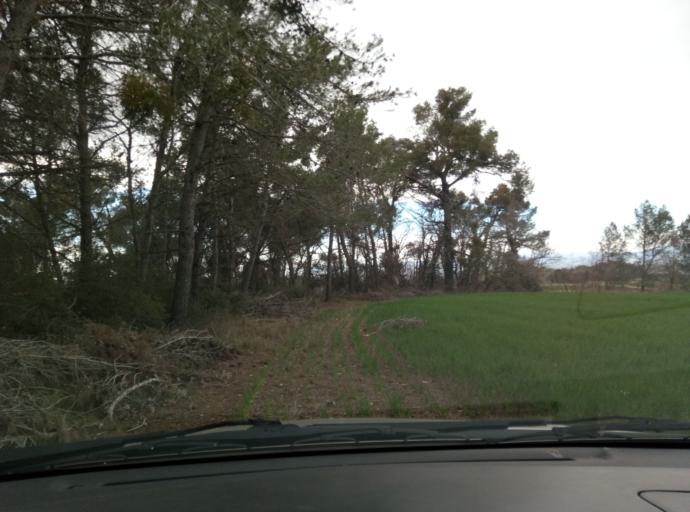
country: ES
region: Catalonia
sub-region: Provincia de Lleida
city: Nalec
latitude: 41.5143
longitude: 1.1394
